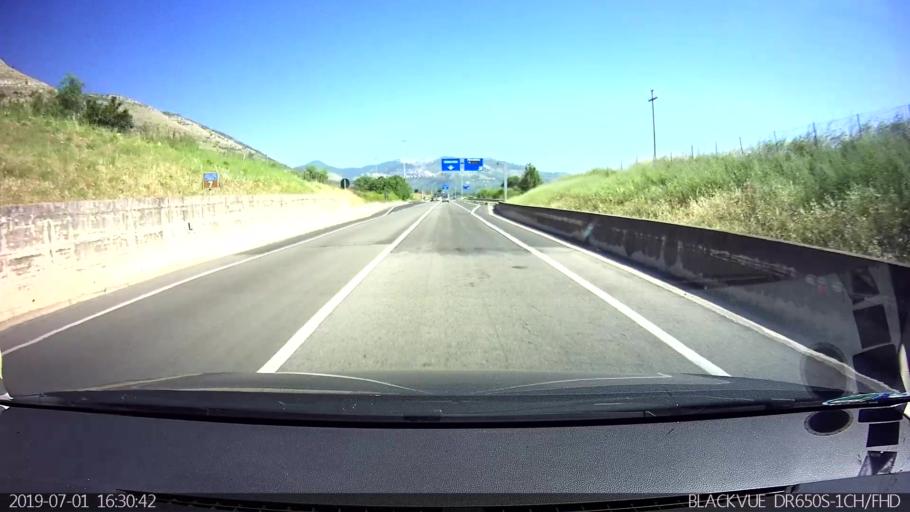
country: IT
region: Latium
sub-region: Provincia di Latina
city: Roccasecca dei Volsci
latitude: 41.4613
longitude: 13.2030
